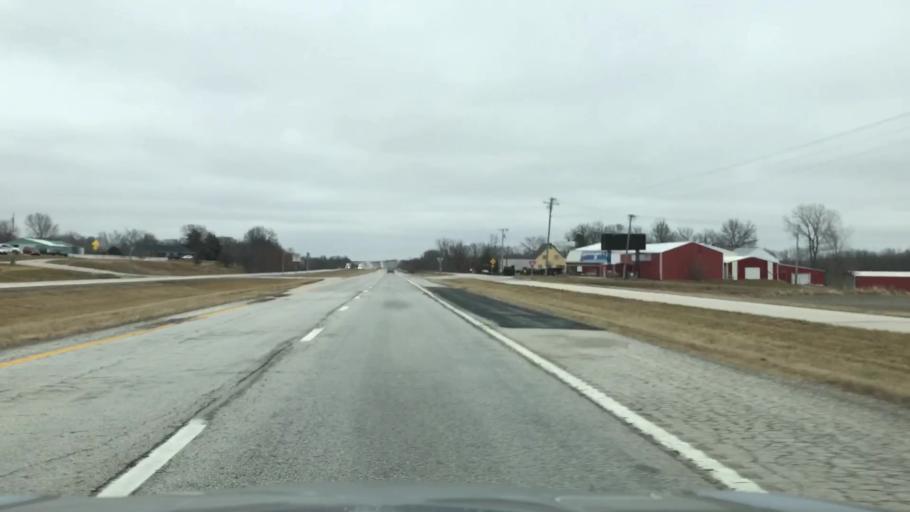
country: US
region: Missouri
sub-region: Linn County
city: Marceline
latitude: 39.7616
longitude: -92.9900
